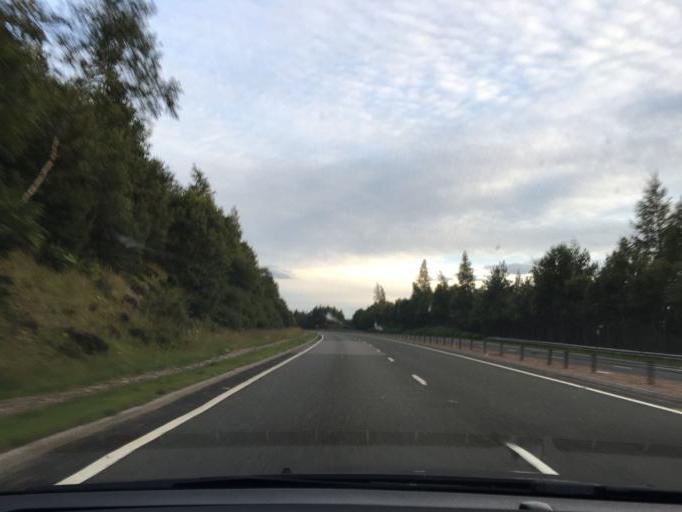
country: GB
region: Scotland
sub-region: Highland
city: Aviemore
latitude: 57.3264
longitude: -3.9780
